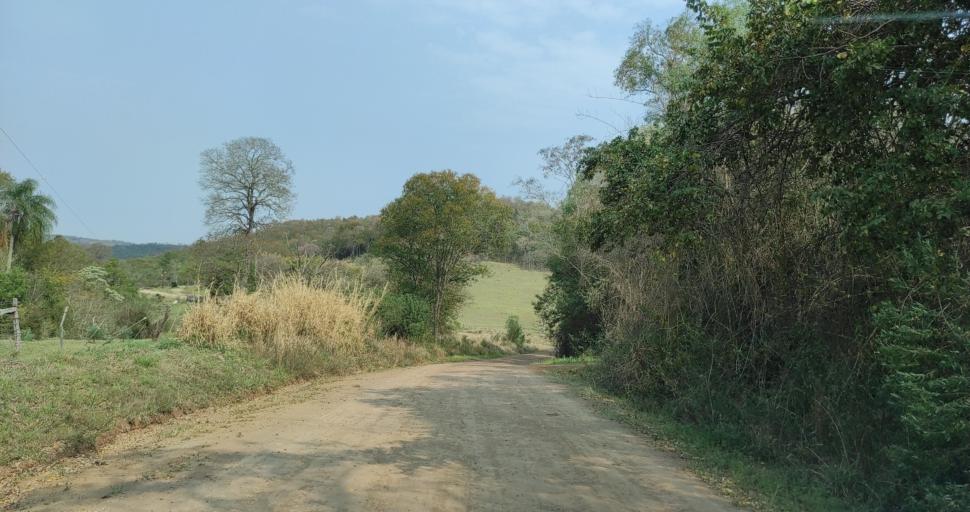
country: AR
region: Misiones
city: Cerro Cora
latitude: -27.5490
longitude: -55.5825
